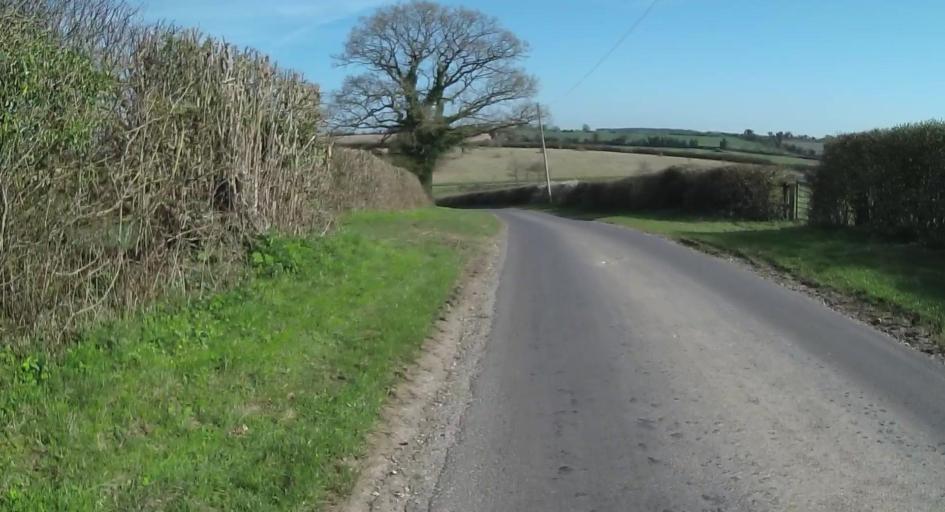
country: GB
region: England
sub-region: Hampshire
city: Highclere
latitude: 51.2604
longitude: -1.3852
